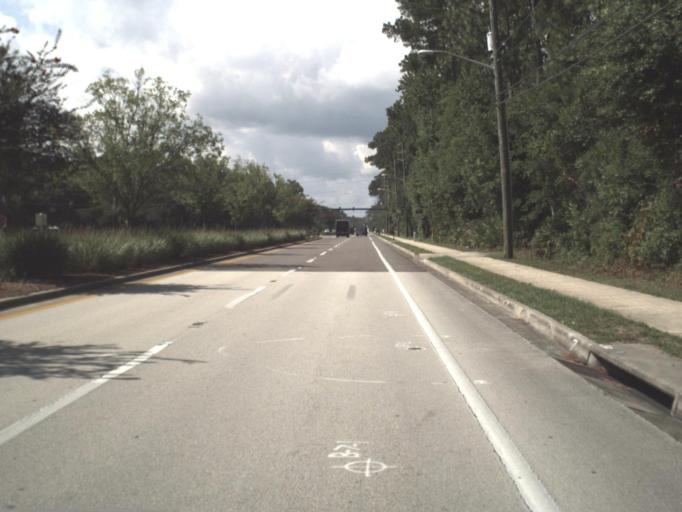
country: US
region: Florida
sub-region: Saint Johns County
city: Fruit Cove
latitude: 30.1097
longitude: -81.6266
